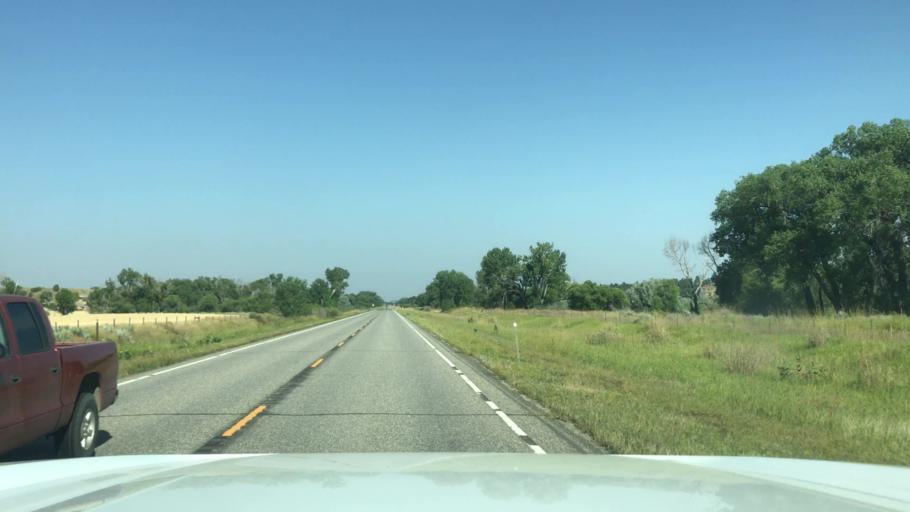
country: US
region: Montana
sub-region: Golden Valley County
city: Ryegate
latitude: 46.3005
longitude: -109.1013
